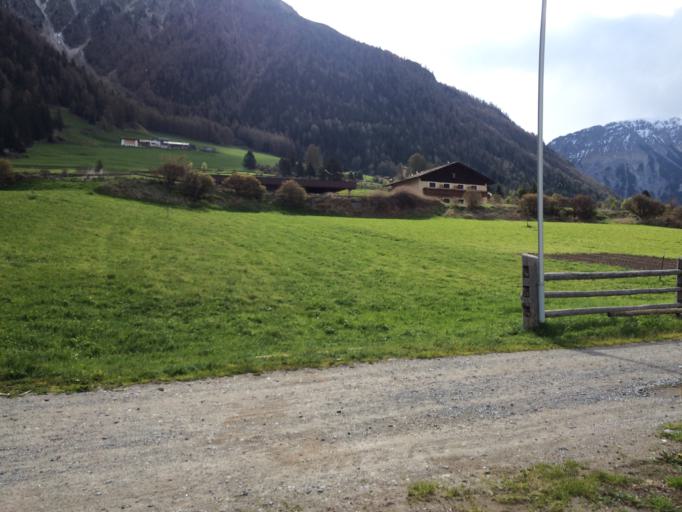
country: IT
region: Trentino-Alto Adige
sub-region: Bolzano
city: Curon Venosta
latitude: 46.8259
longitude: 10.5203
